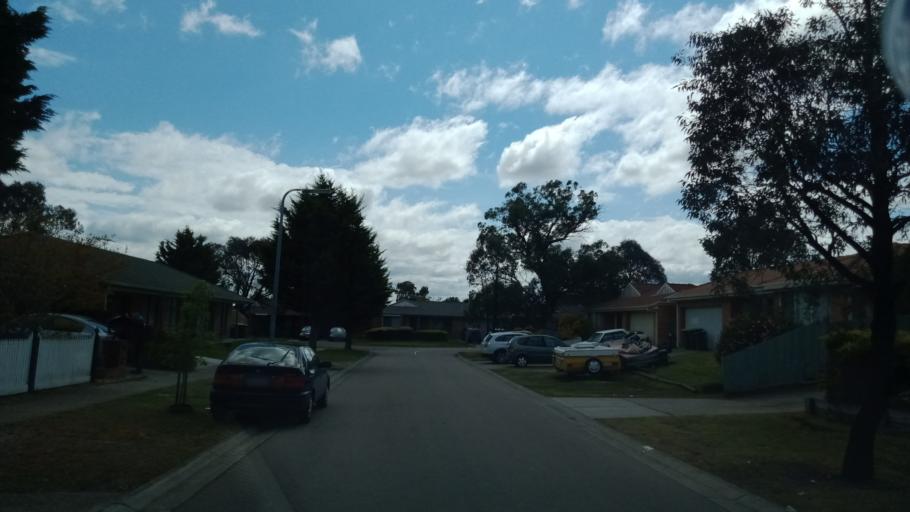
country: AU
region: Victoria
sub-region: Frankston
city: Sandhurst
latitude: -38.0916
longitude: 145.1941
